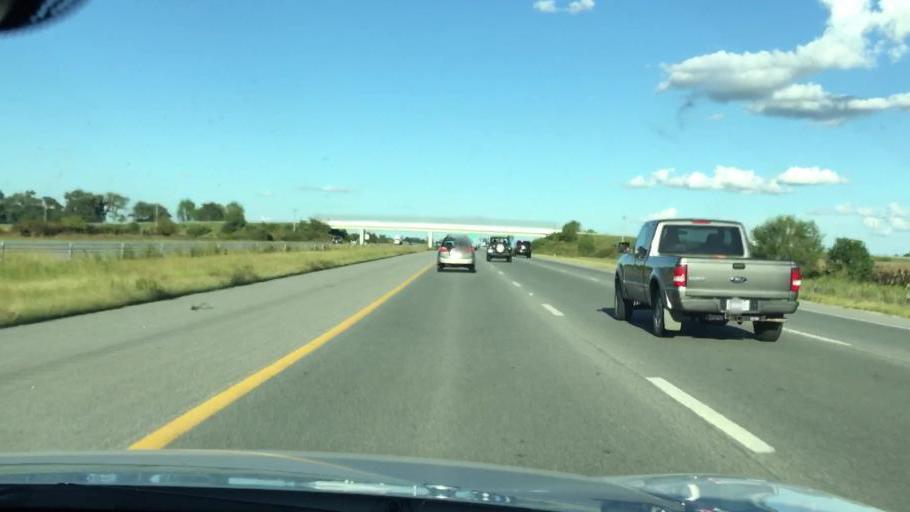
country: US
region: Ohio
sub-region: Madison County
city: London
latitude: 39.9506
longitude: -83.4074
